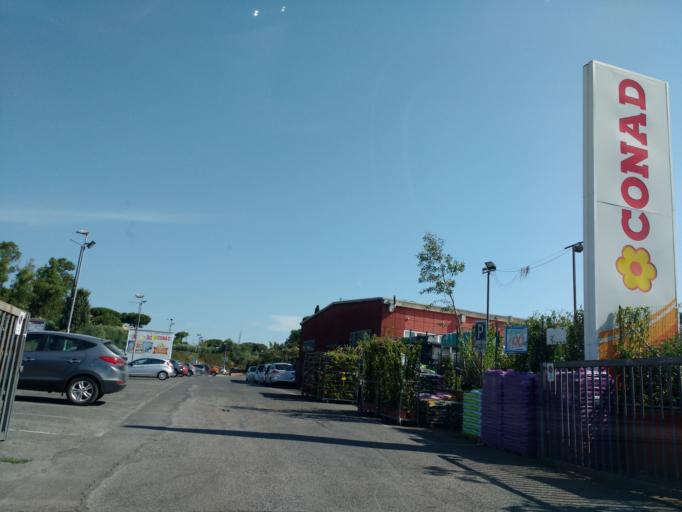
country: IT
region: Latium
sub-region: Citta metropolitana di Roma Capitale
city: Borgo Lotti
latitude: 41.8033
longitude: 12.5356
